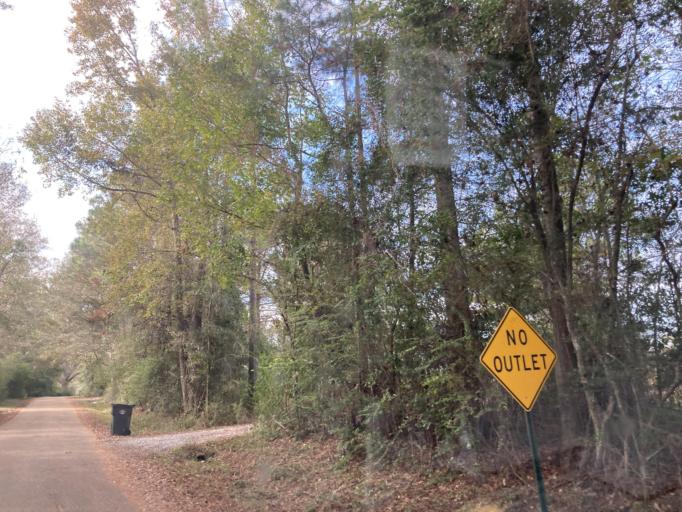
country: US
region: Mississippi
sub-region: Lamar County
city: Purvis
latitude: 31.2221
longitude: -89.3686
